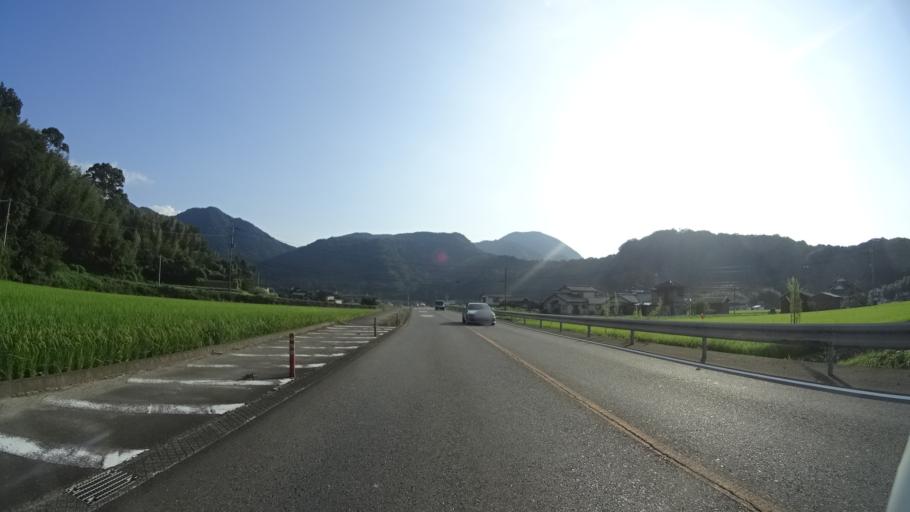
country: JP
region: Oita
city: Bungo-Takada-shi
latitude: 33.5005
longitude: 131.3262
